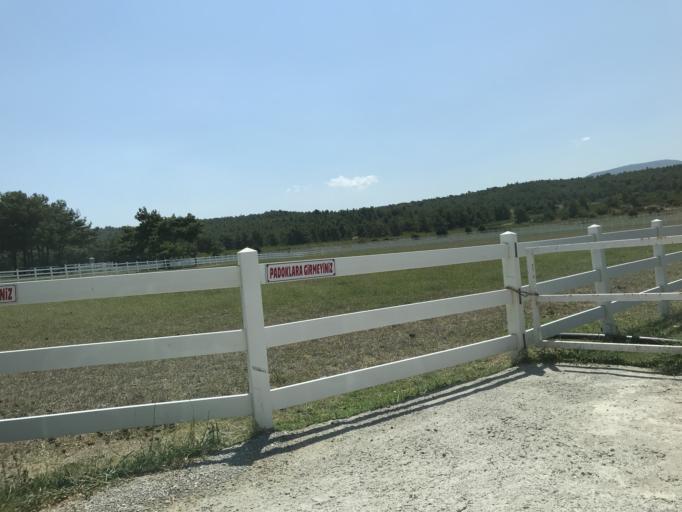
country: TR
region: Izmir
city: Urla
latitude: 38.2888
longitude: 26.7218
